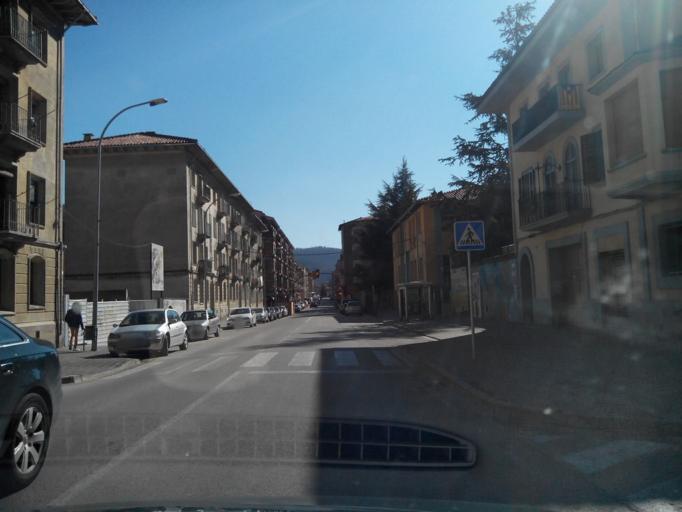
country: ES
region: Catalonia
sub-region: Provincia de Girona
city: Ripoll
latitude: 42.1962
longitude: 2.1918
